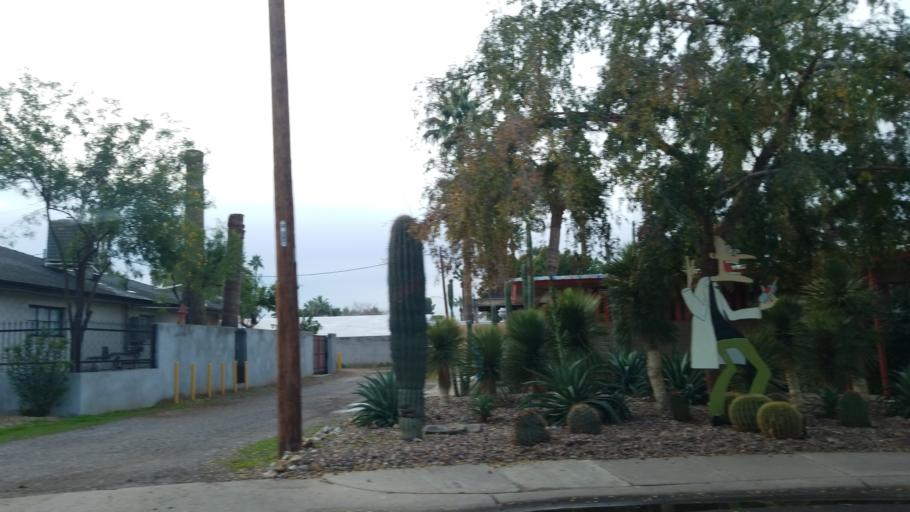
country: US
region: Arizona
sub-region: Maricopa County
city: Phoenix
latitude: 33.4786
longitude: -112.0847
